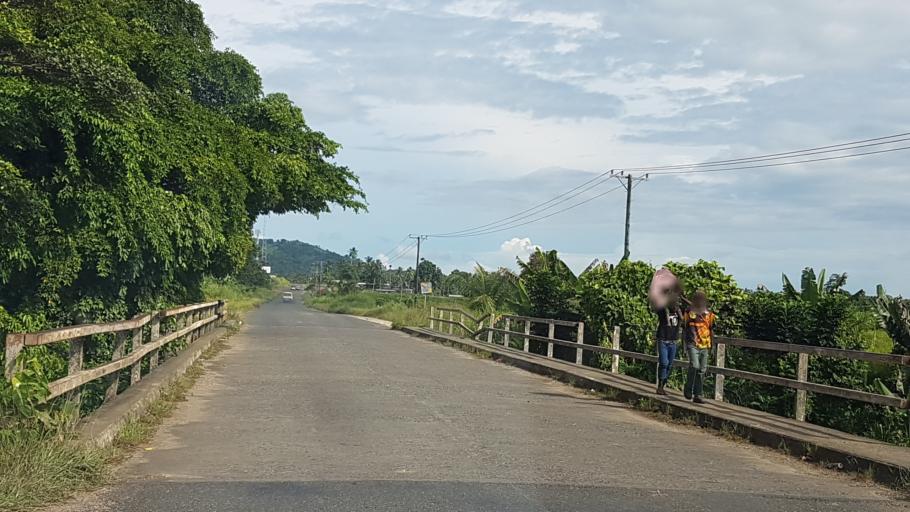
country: PG
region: Madang
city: Madang
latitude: -5.2150
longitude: 145.7758
